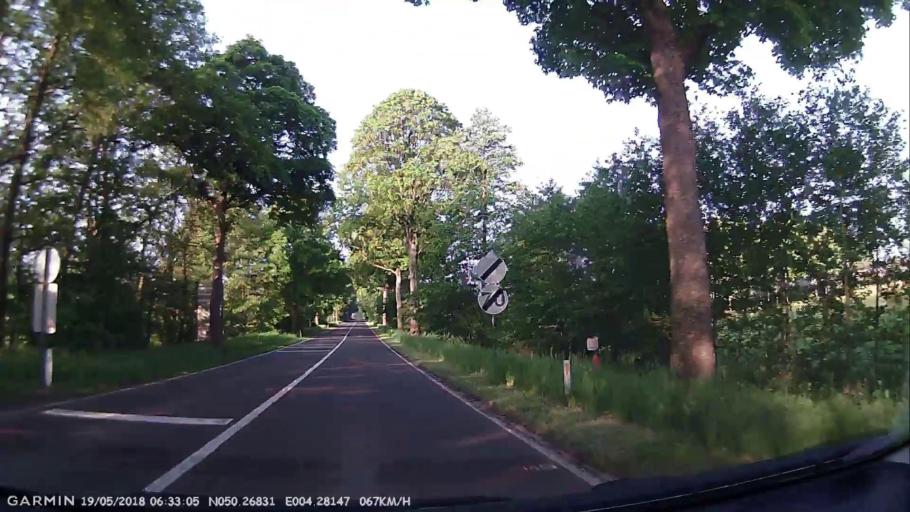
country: BE
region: Wallonia
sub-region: Province du Hainaut
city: Beaumont
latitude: 50.2683
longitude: 4.2815
